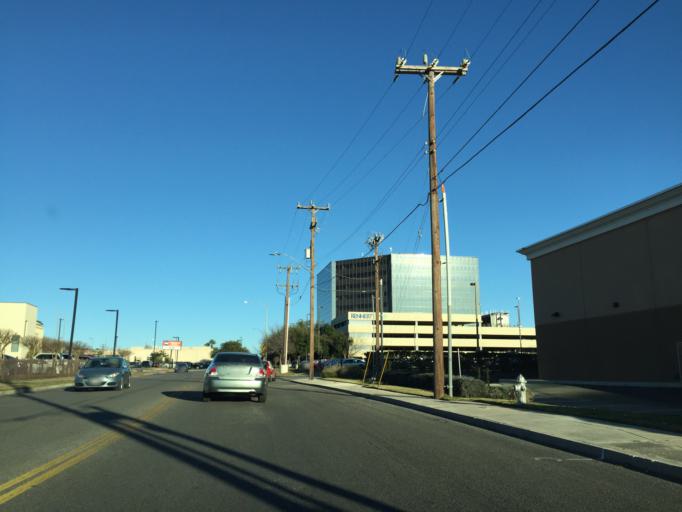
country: US
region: Texas
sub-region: Bexar County
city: Castle Hills
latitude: 29.5228
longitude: -98.5042
